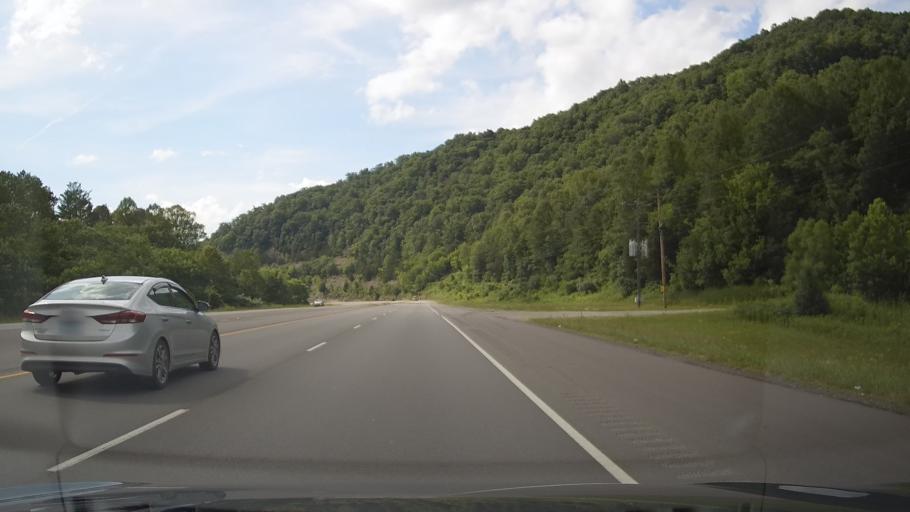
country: US
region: Kentucky
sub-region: Floyd County
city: Prestonsburg
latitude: 37.6088
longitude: -82.7046
